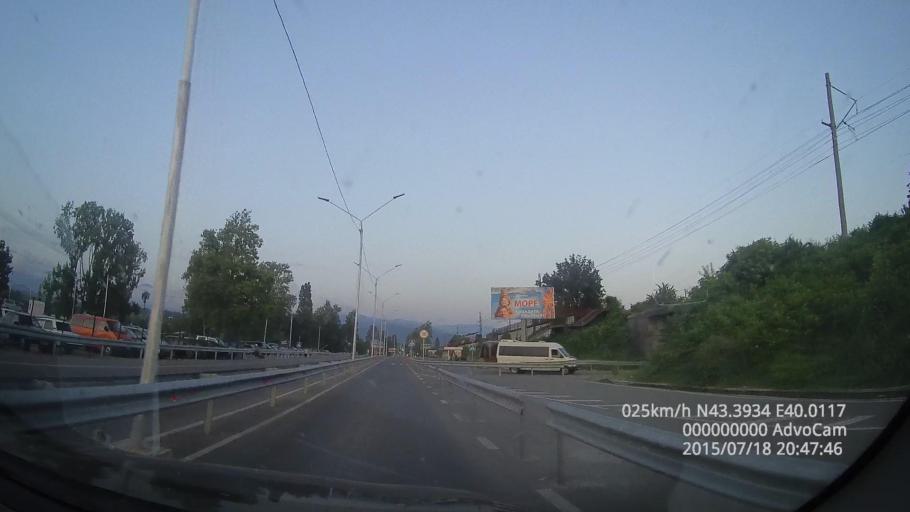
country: GE
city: Gantiadi
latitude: 43.3933
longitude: 40.0124
